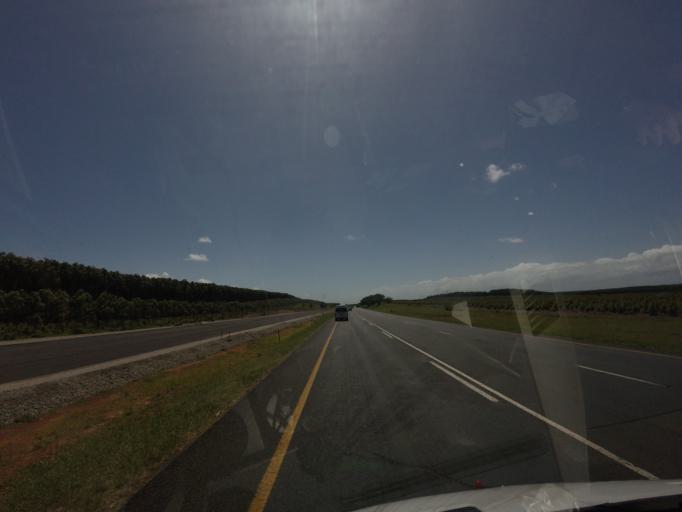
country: ZA
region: KwaZulu-Natal
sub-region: uThungulu District Municipality
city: eSikhawini
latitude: -28.8917
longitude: 31.8413
